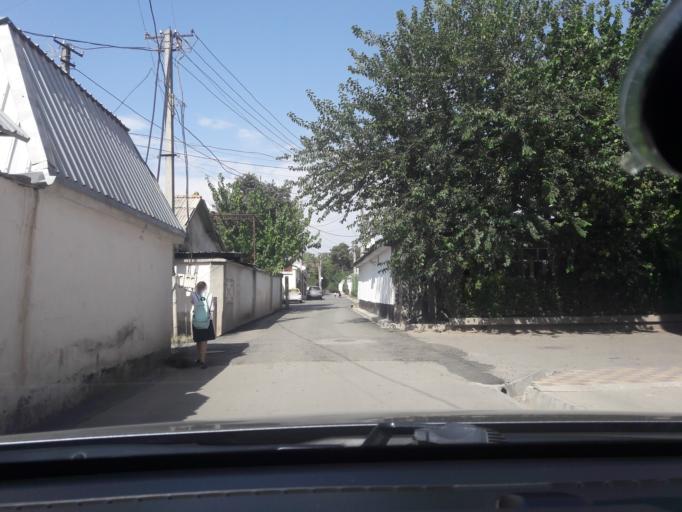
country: TJ
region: Dushanbe
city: Dushanbe
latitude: 38.5755
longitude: 68.7969
